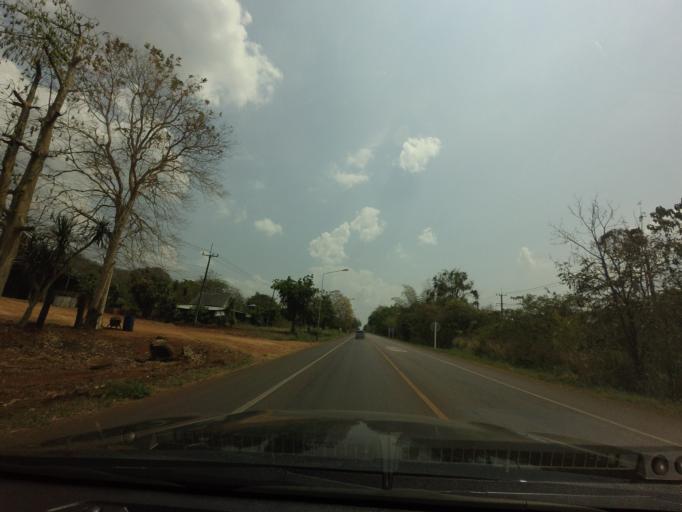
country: TH
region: Kanchanaburi
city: Sai Yok
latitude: 14.1343
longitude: 99.1558
